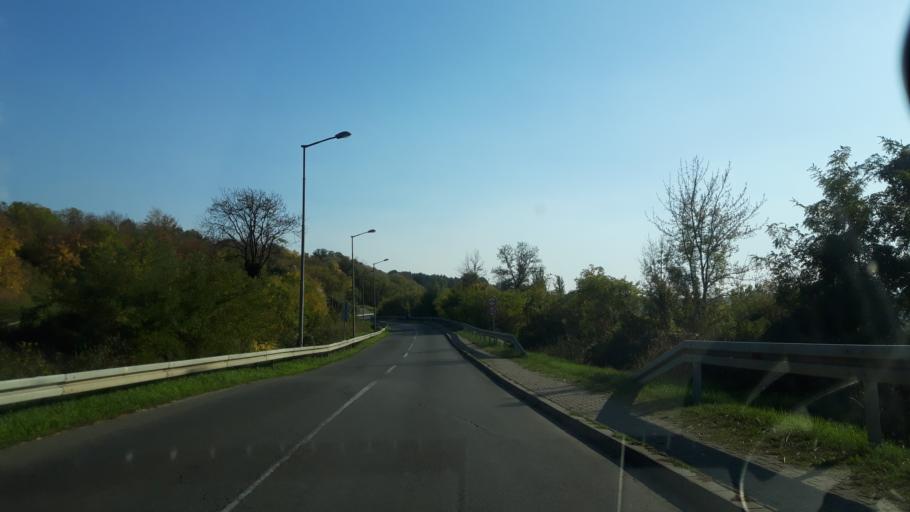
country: RS
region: Autonomna Pokrajina Vojvodina
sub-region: Juznobacki Okrug
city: Petrovaradin
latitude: 45.2476
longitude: 19.8655
